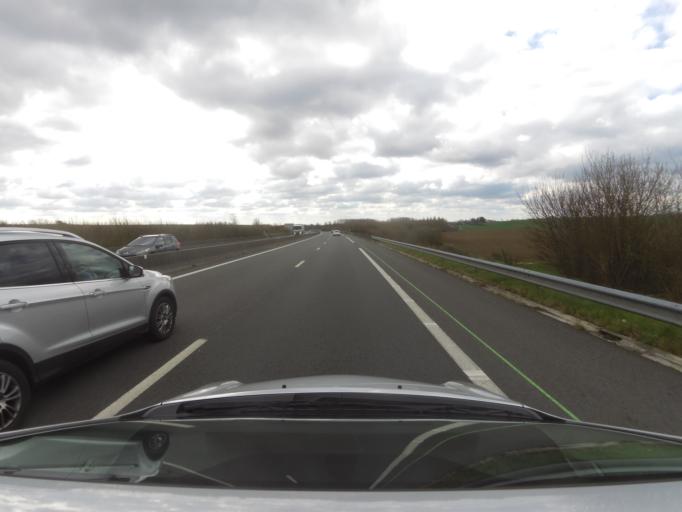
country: FR
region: Picardie
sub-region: Departement de la Somme
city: Quend
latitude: 50.3526
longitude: 1.6887
